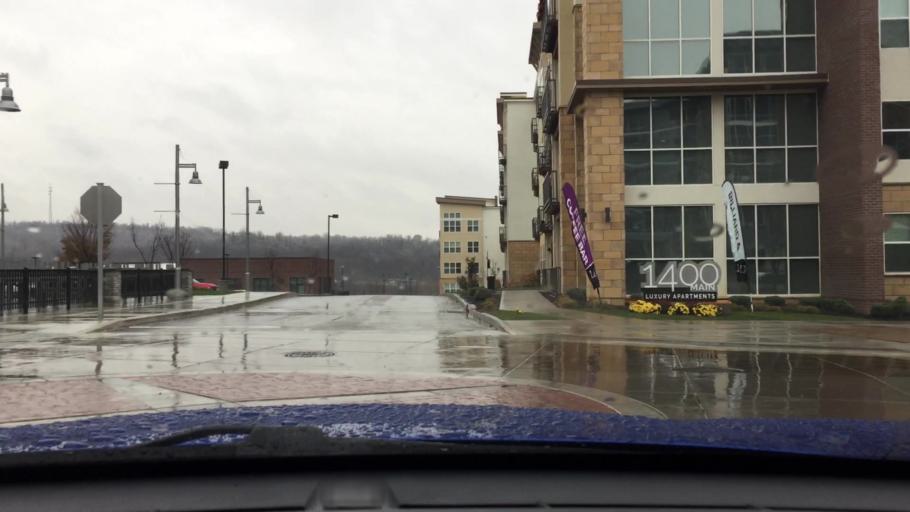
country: US
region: Pennsylvania
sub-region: Washington County
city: Canonsburg
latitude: 40.2751
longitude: -80.1664
